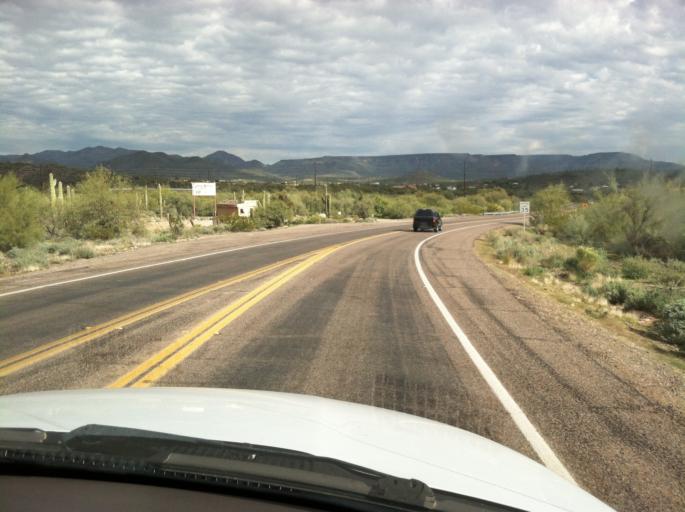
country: US
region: Arizona
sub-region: Maricopa County
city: New River
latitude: 33.9136
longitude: -112.1453
